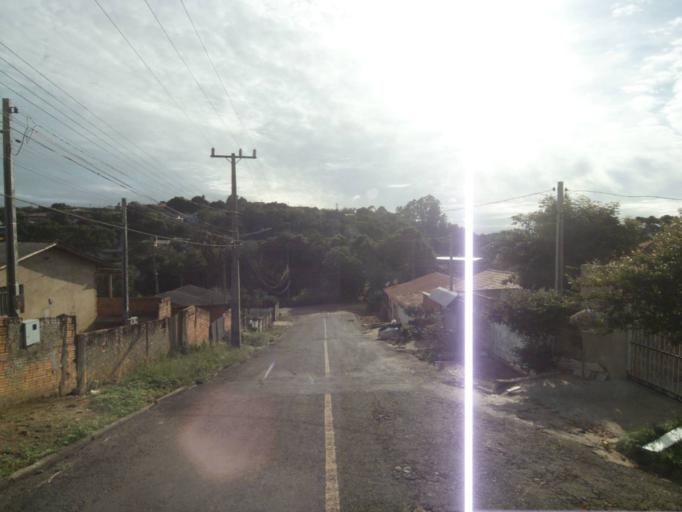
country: BR
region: Parana
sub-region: Telemaco Borba
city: Telemaco Borba
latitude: -24.3414
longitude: -50.6161
